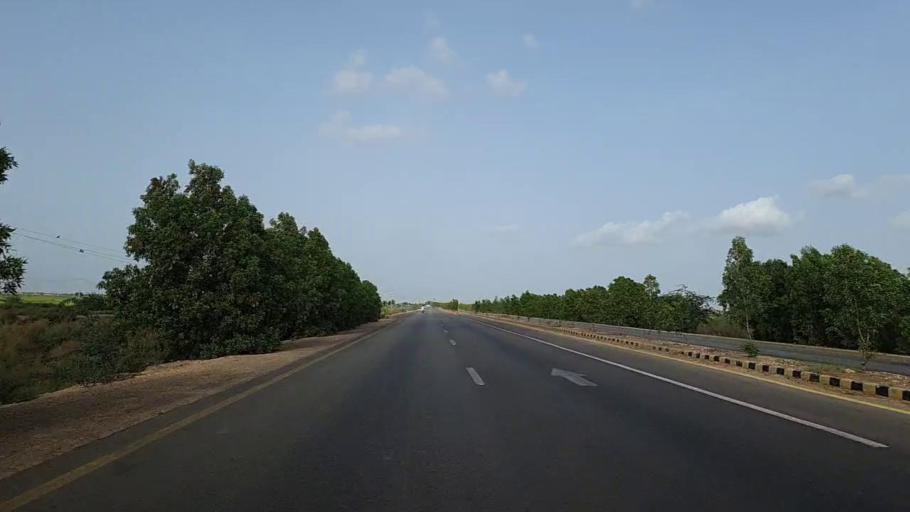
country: PK
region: Sindh
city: Thatta
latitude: 24.7446
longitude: 67.8487
